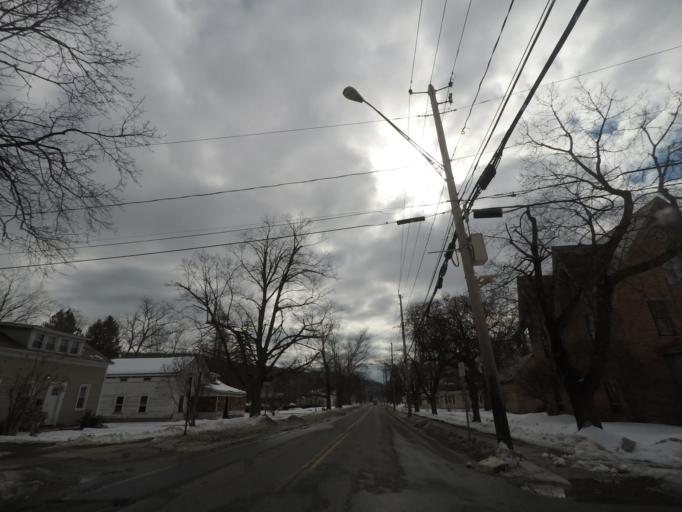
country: US
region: New York
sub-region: Washington County
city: Cambridge
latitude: 43.0262
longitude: -73.3760
